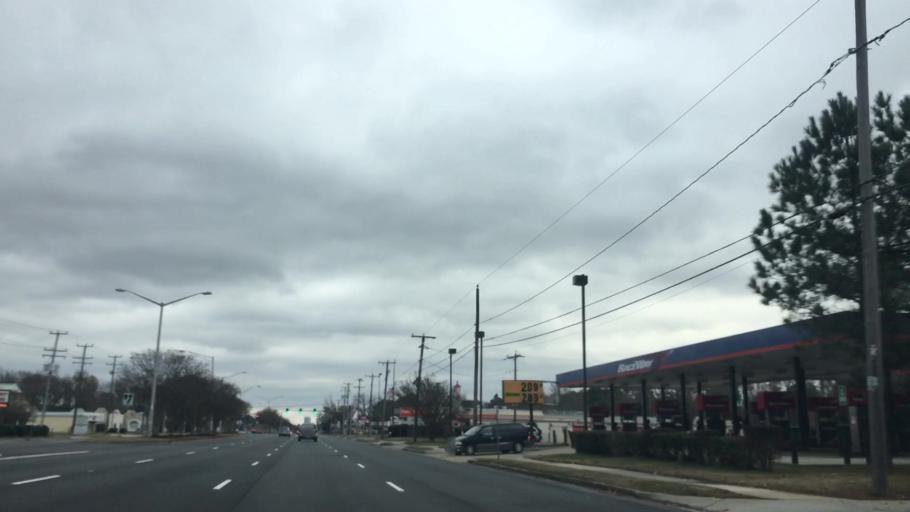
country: US
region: Virginia
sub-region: City of Chesapeake
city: Chesapeake
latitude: 36.8528
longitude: -76.1743
